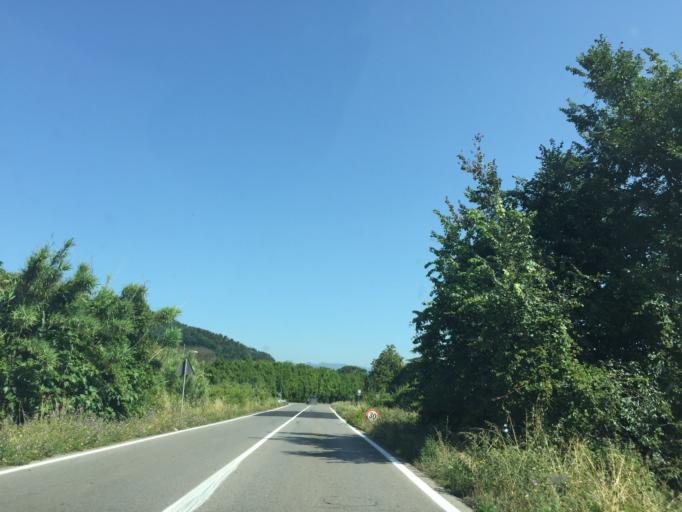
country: IT
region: Tuscany
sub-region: Provincia di Lucca
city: Lucca
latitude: 43.8030
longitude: 10.4846
